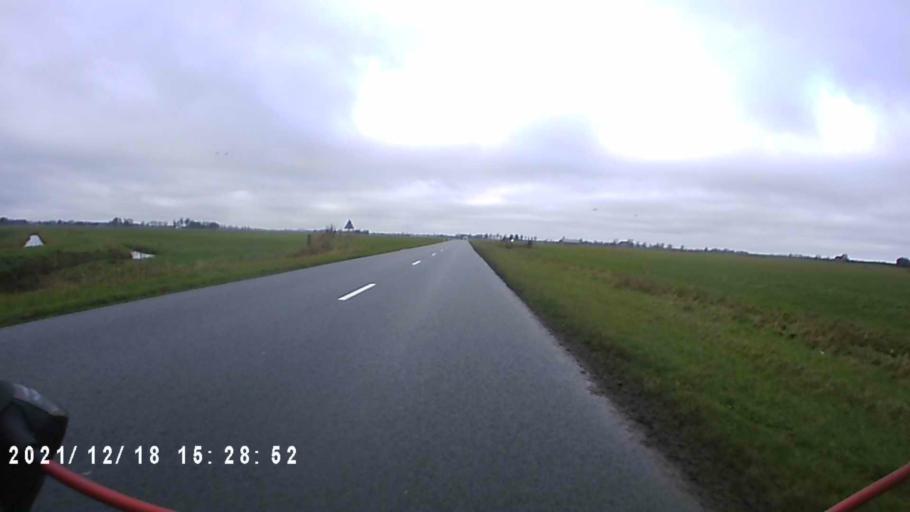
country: NL
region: Friesland
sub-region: Gemeente Dongeradeel
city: Anjum
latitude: 53.3331
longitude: 6.1434
